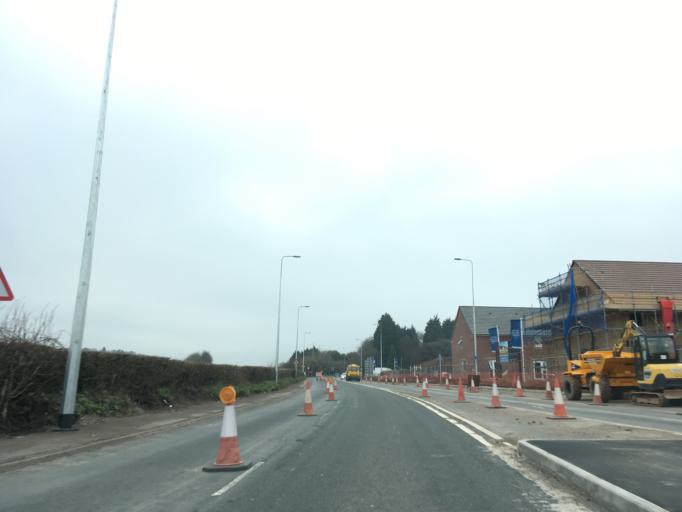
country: GB
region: Wales
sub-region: Newport
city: Marshfield
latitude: 51.5340
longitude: -3.0952
